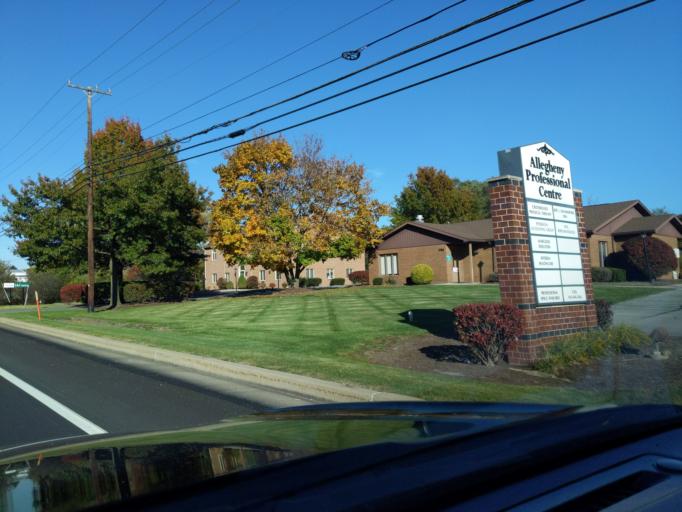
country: US
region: Pennsylvania
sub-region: Blair County
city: Hollidaysburg
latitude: 40.4443
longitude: -78.4113
